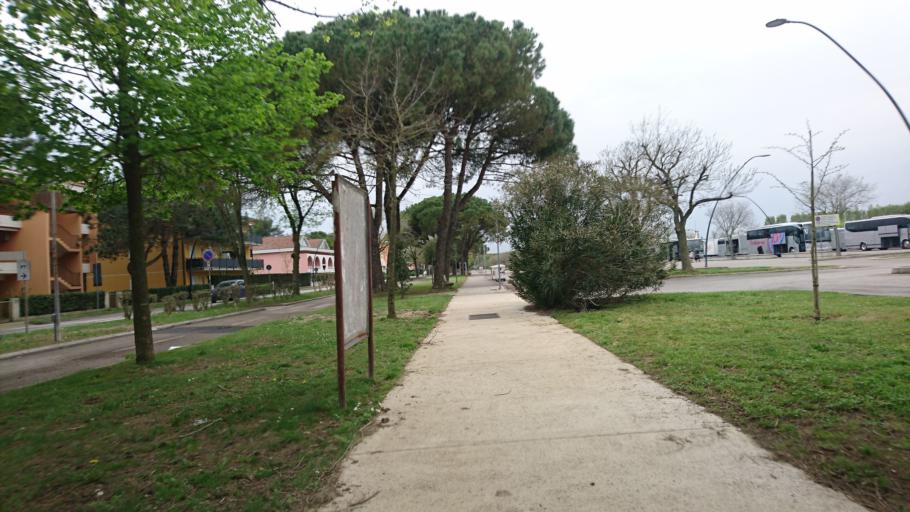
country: IT
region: Veneto
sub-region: Provincia di Venezia
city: Bibione
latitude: 45.6384
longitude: 13.0534
